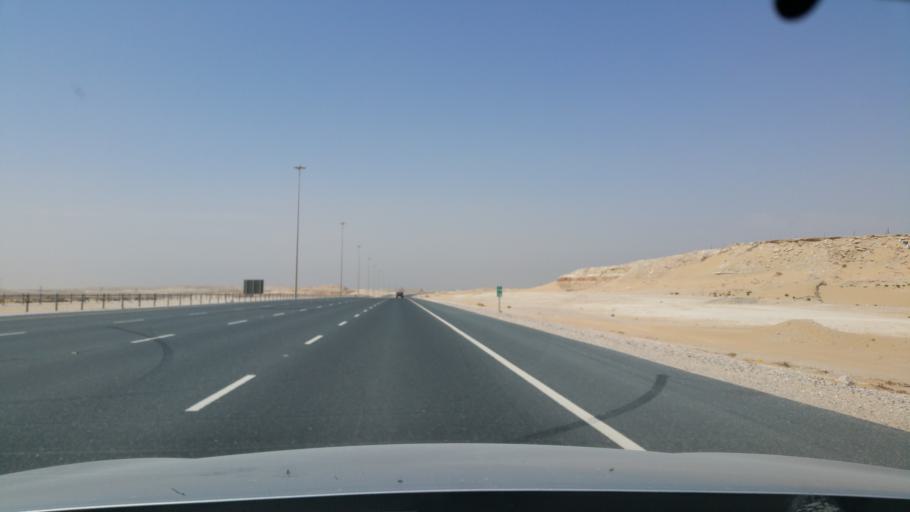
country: QA
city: Umm Bab
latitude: 24.8697
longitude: 50.9124
